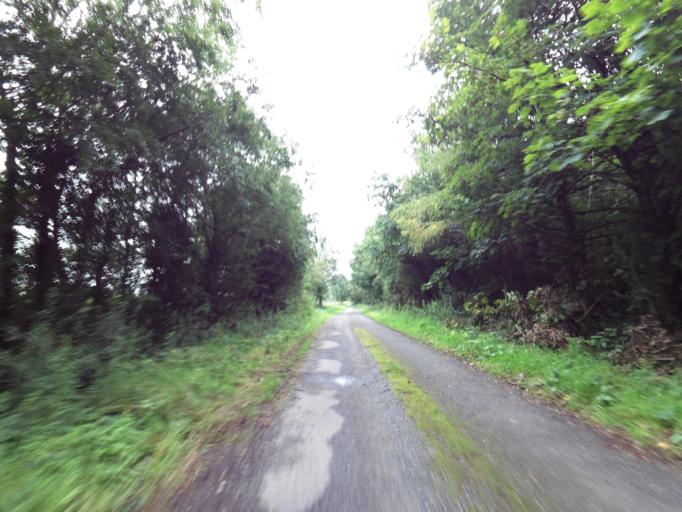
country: IE
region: Leinster
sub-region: Uibh Fhaili
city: Ferbane
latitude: 53.2395
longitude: -7.7389
